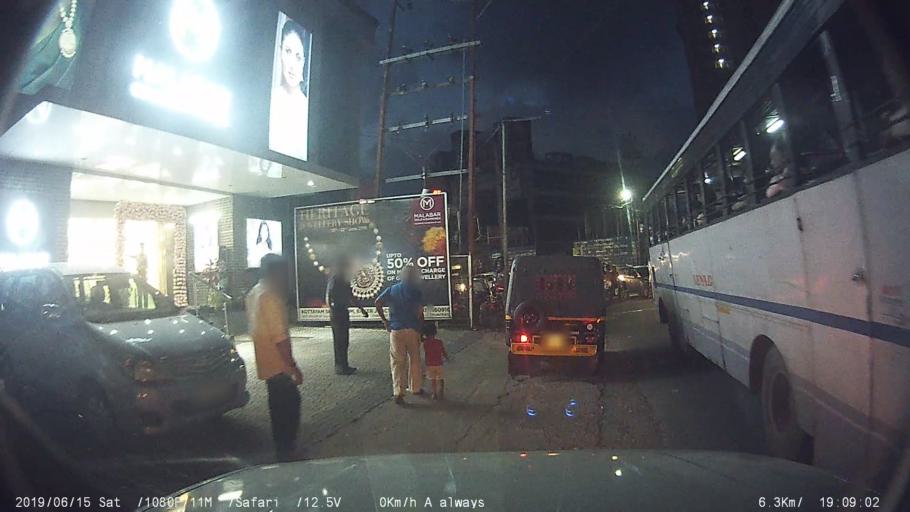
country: IN
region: Kerala
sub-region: Kottayam
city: Kottayam
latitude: 9.5929
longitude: 76.5221
